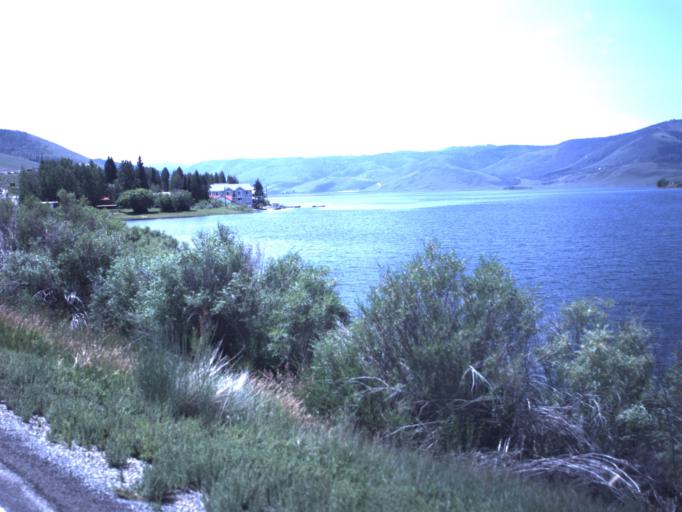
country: US
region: Utah
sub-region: Carbon County
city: Helper
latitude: 39.7975
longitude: -111.1325
